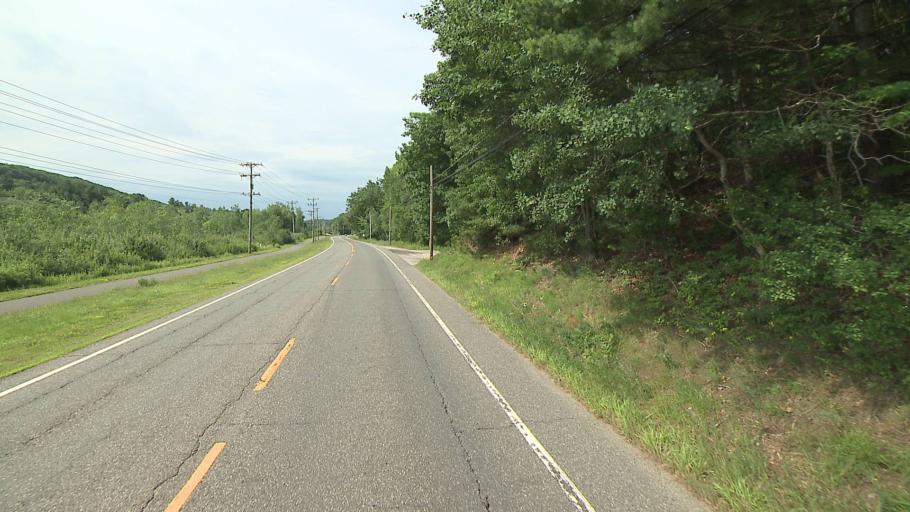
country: US
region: Connecticut
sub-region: Litchfield County
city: Winchester Center
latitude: 41.8566
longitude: -73.0930
